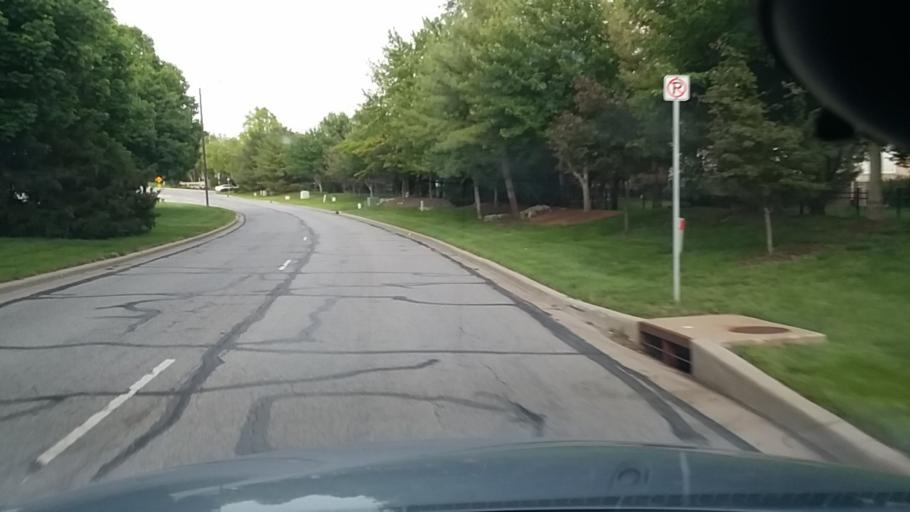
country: US
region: Kansas
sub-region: Johnson County
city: Olathe
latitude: 38.9504
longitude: -94.8146
